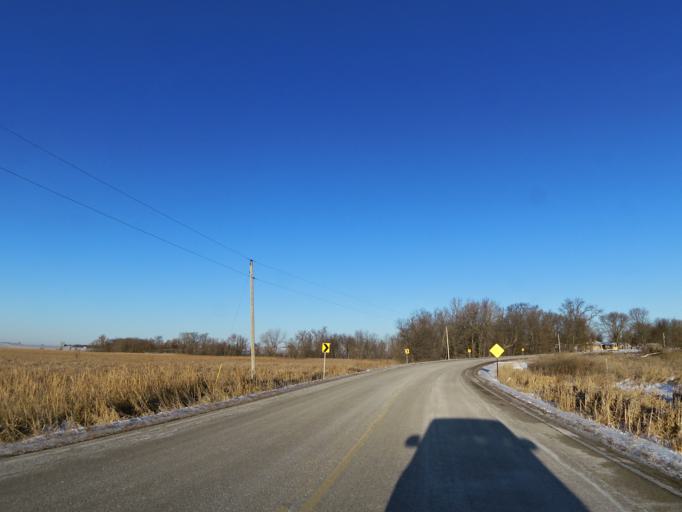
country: US
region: Minnesota
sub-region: Scott County
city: Jordan
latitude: 44.6590
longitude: -93.5303
